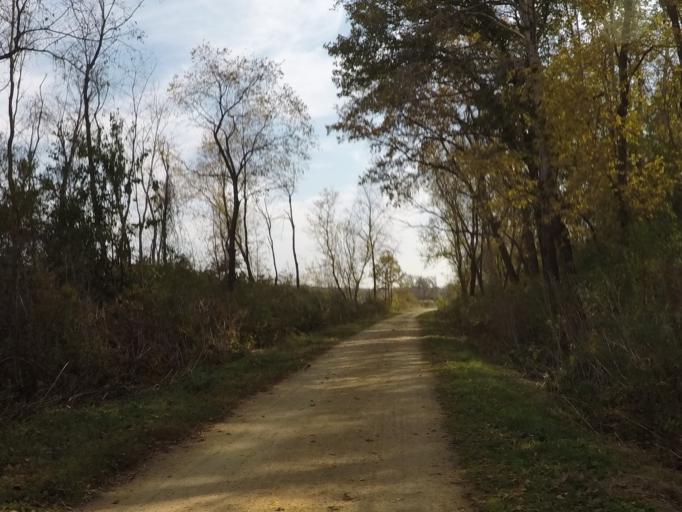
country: US
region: Wisconsin
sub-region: Dane County
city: Cross Plains
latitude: 43.0273
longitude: -89.6374
